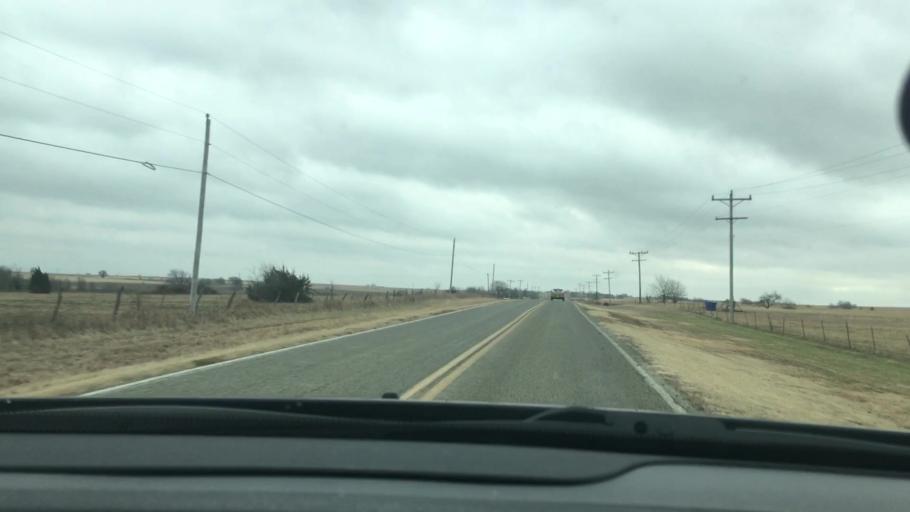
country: US
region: Oklahoma
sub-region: Johnston County
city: Tishomingo
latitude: 34.1434
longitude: -96.5352
